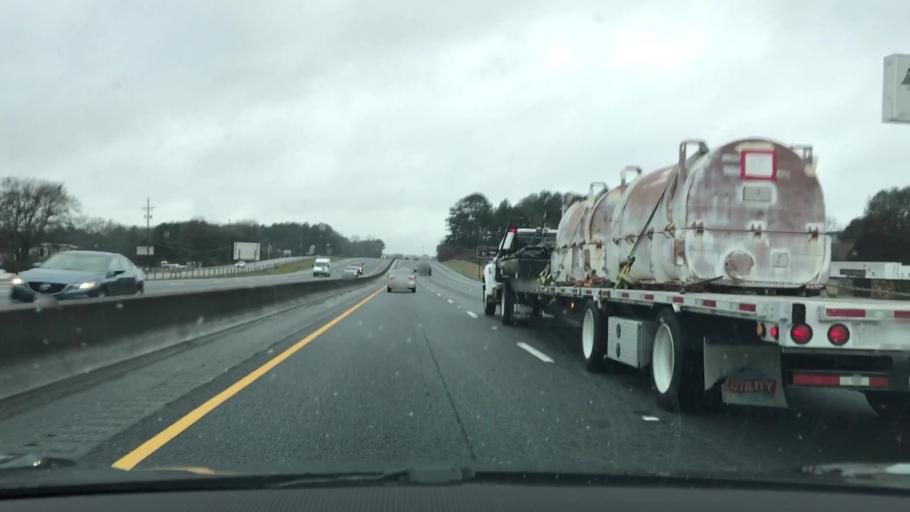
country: US
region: Georgia
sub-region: Newton County
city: Oxford
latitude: 33.6135
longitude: -83.9041
